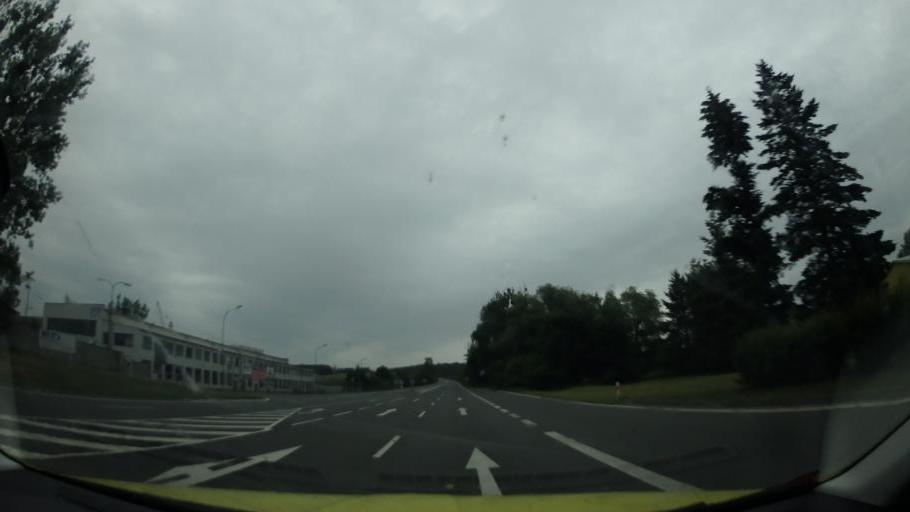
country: CZ
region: Olomoucky
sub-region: Okres Prerov
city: Hranice
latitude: 49.5630
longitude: 17.7605
